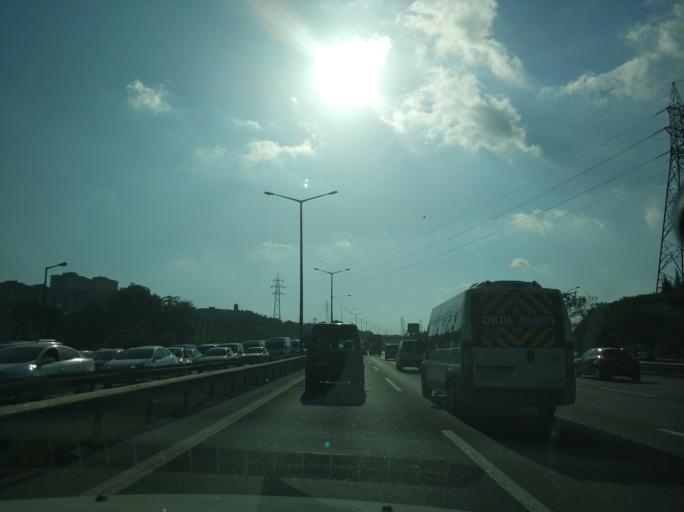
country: TR
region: Istanbul
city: Sisli
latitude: 41.0999
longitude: 28.9752
